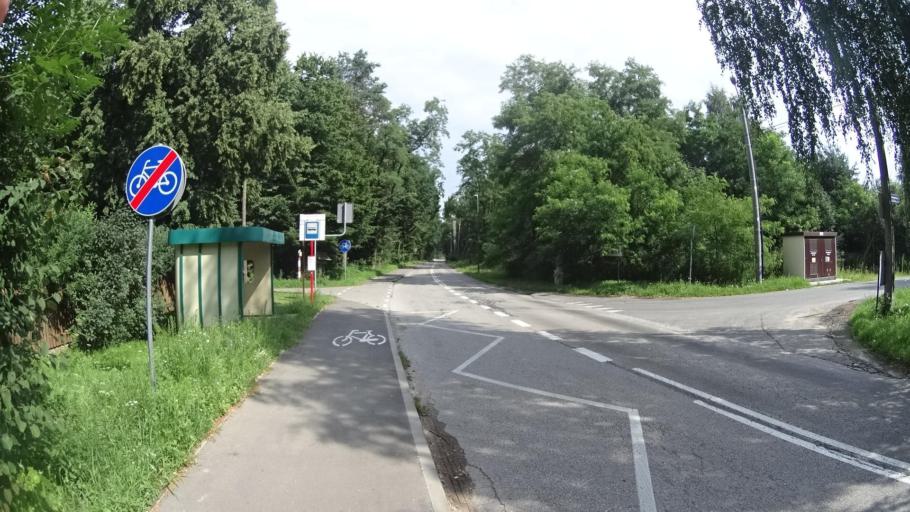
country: PL
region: Masovian Voivodeship
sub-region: Powiat pruszkowski
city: Nadarzyn
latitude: 52.0300
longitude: 20.7830
